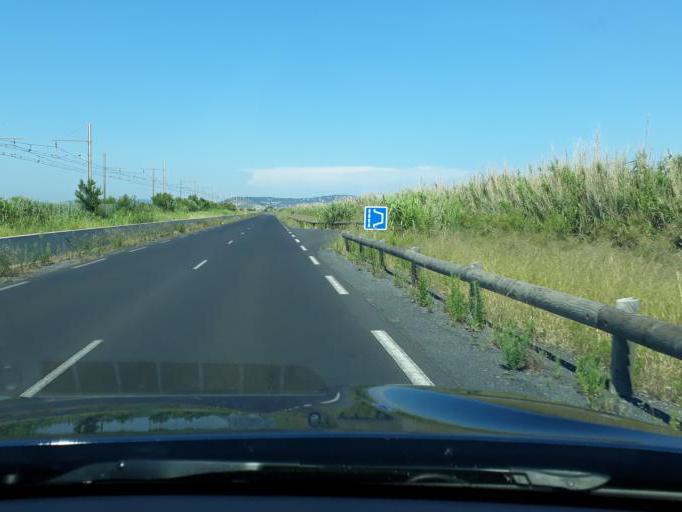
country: FR
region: Languedoc-Roussillon
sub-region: Departement de l'Herault
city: Meze
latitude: 43.3633
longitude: 3.6085
